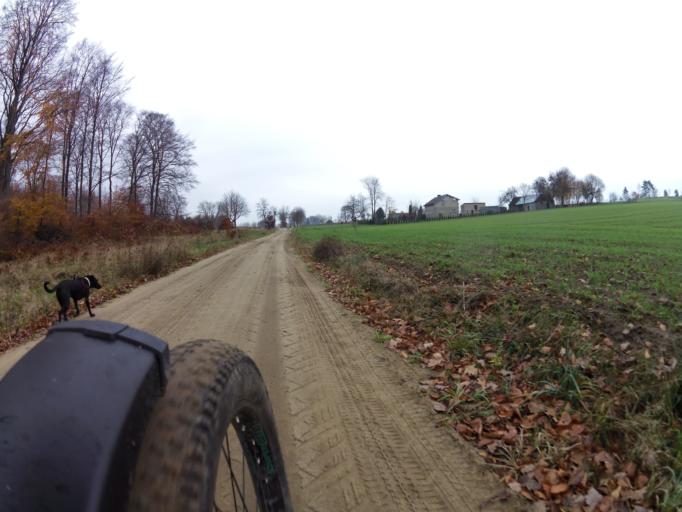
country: PL
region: Pomeranian Voivodeship
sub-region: Powiat pucki
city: Krokowa
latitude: 54.7163
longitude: 18.1388
